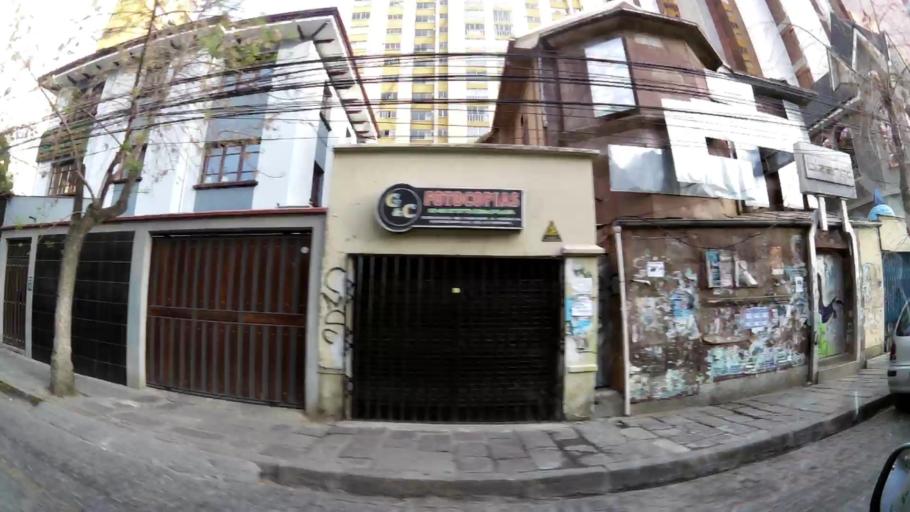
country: BO
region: La Paz
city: La Paz
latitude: -16.5080
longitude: -68.1284
